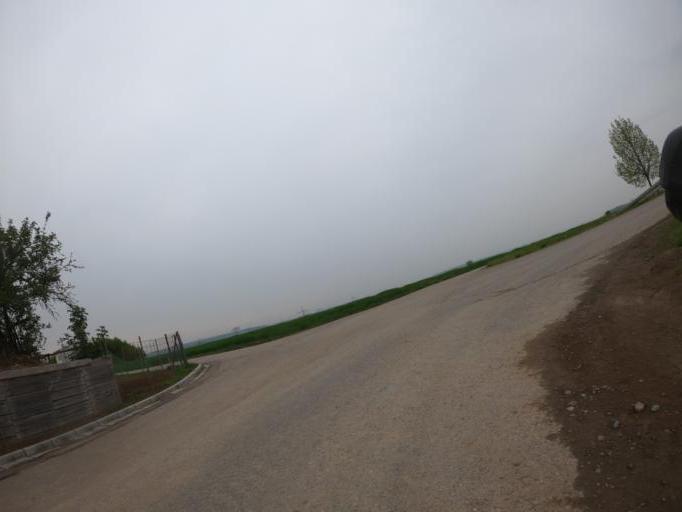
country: DE
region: Baden-Wuerttemberg
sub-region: Regierungsbezirk Stuttgart
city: Bietigheim-Bissingen
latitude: 48.9517
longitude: 9.0763
